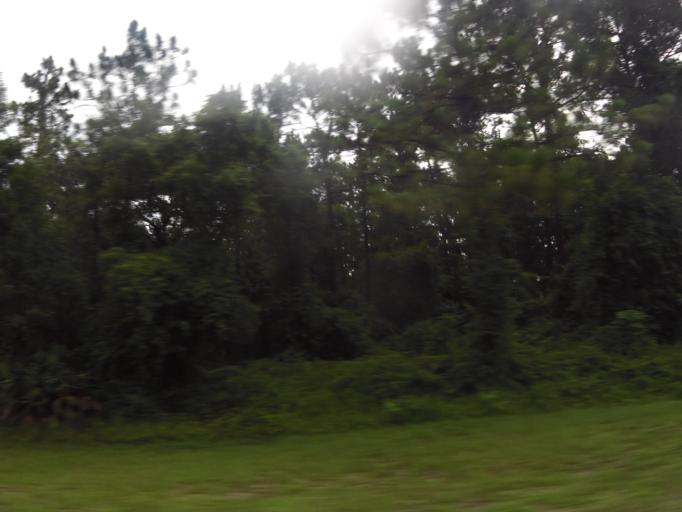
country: US
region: Florida
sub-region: Duval County
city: Jacksonville Beach
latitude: 30.2608
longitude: -81.5011
